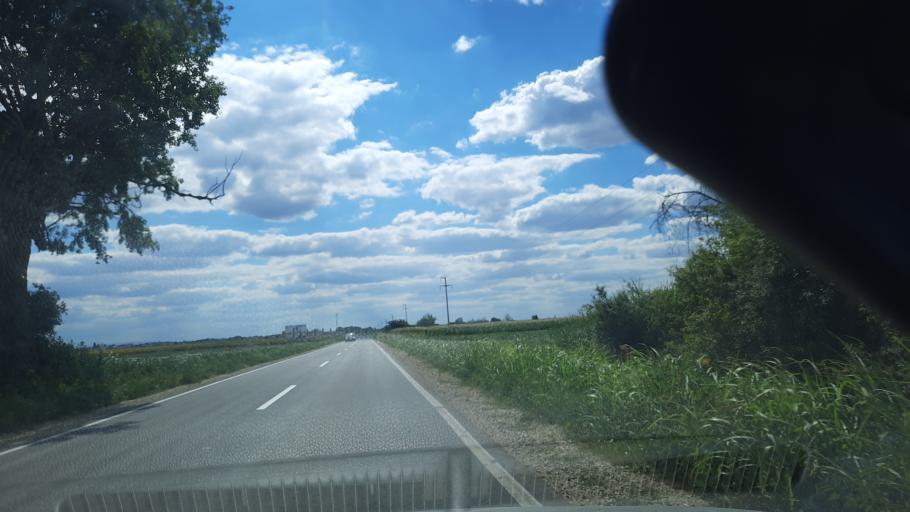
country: RS
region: Autonomna Pokrajina Vojvodina
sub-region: Sremski Okrug
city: Pecinci
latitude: 44.9242
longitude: 19.9894
